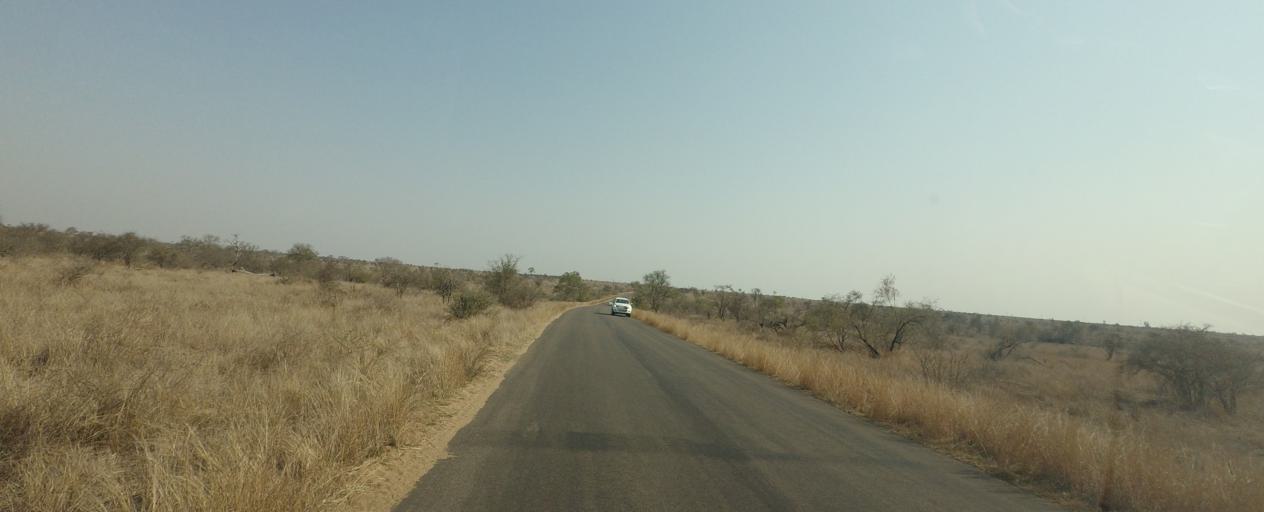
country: ZA
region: Limpopo
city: Thulamahashi
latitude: -24.3651
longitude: 31.7641
